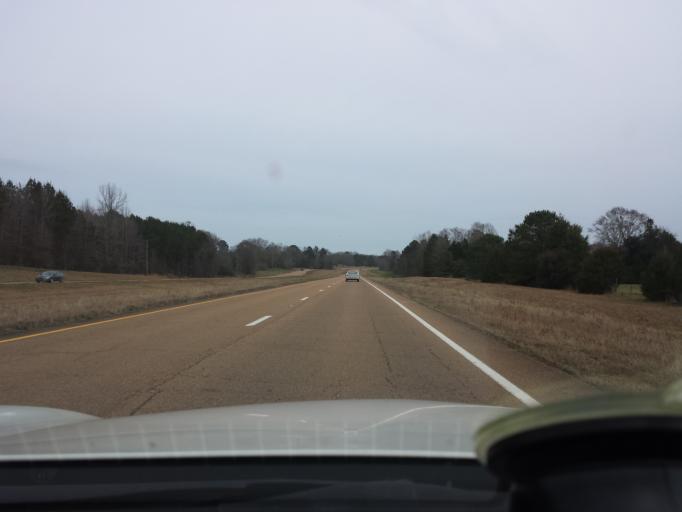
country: US
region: Mississippi
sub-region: Leake County
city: Carthage
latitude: 32.8469
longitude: -89.4612
